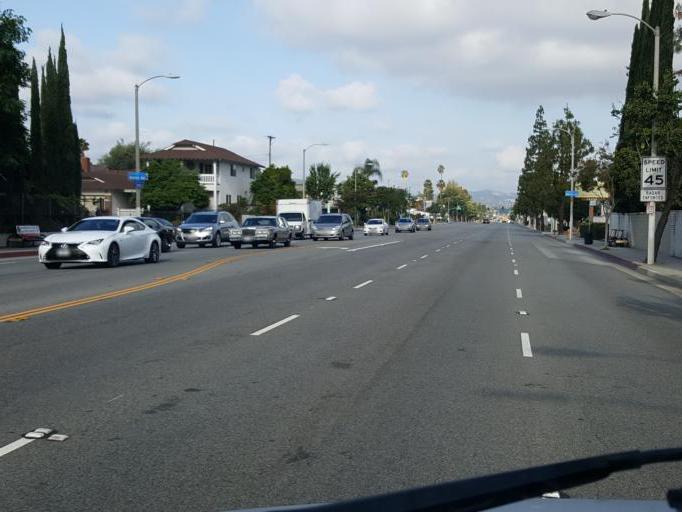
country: US
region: California
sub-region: Los Angeles County
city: Rowland Heights
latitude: 33.9871
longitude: -117.8808
